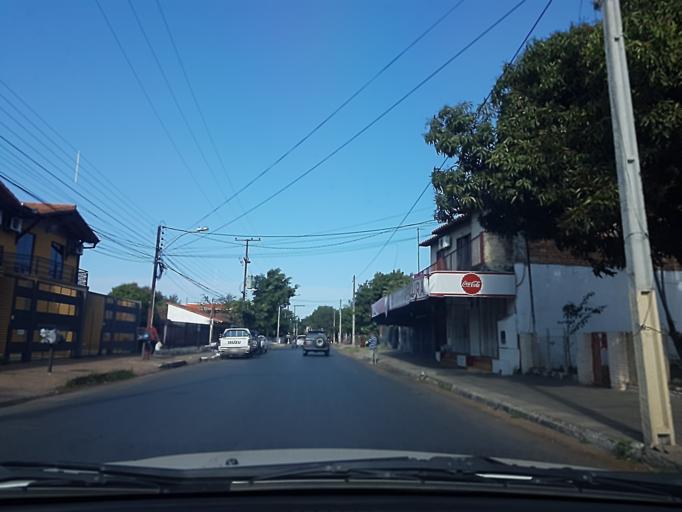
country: PY
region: Central
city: Colonia Mariano Roque Alonso
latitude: -25.2415
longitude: -57.5423
